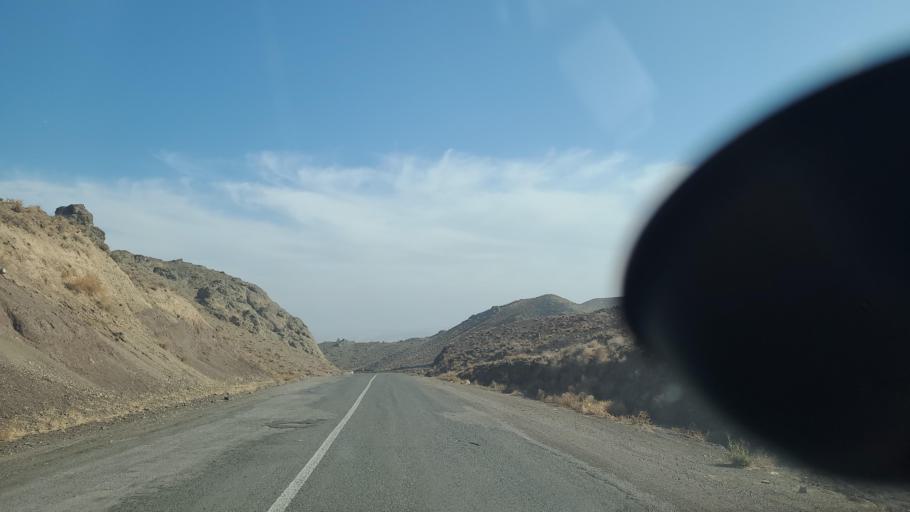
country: IR
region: Razavi Khorasan
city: Fariman
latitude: 35.5938
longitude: 59.7184
